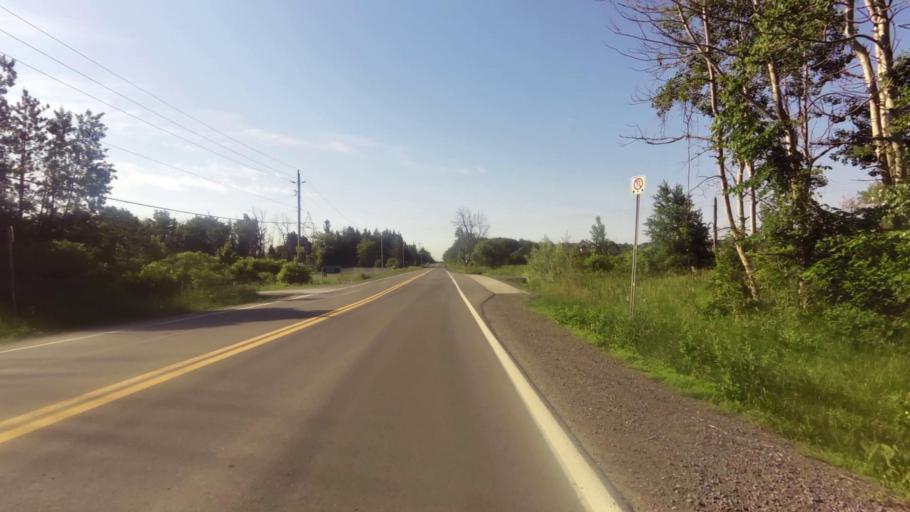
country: CA
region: Ontario
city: Ottawa
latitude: 45.2573
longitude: -75.5676
